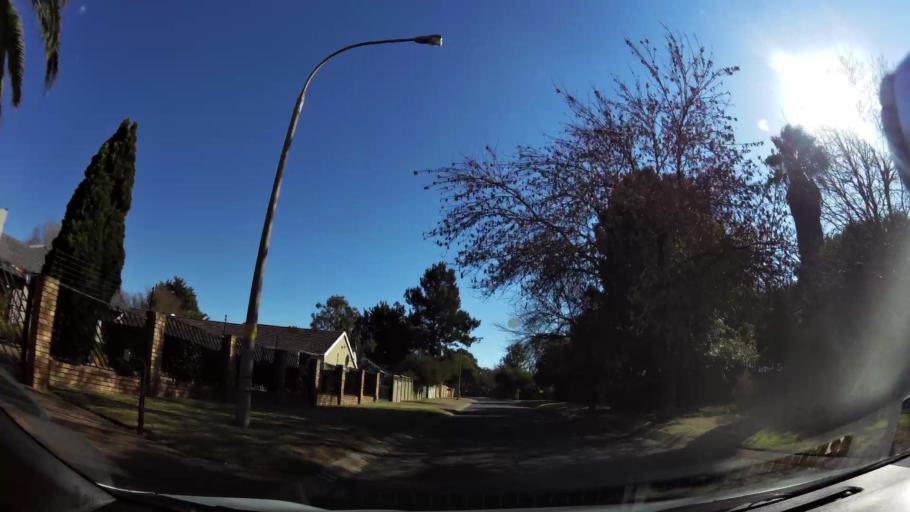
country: ZA
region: Gauteng
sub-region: Ekurhuleni Metropolitan Municipality
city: Germiston
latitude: -26.3320
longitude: 28.1012
